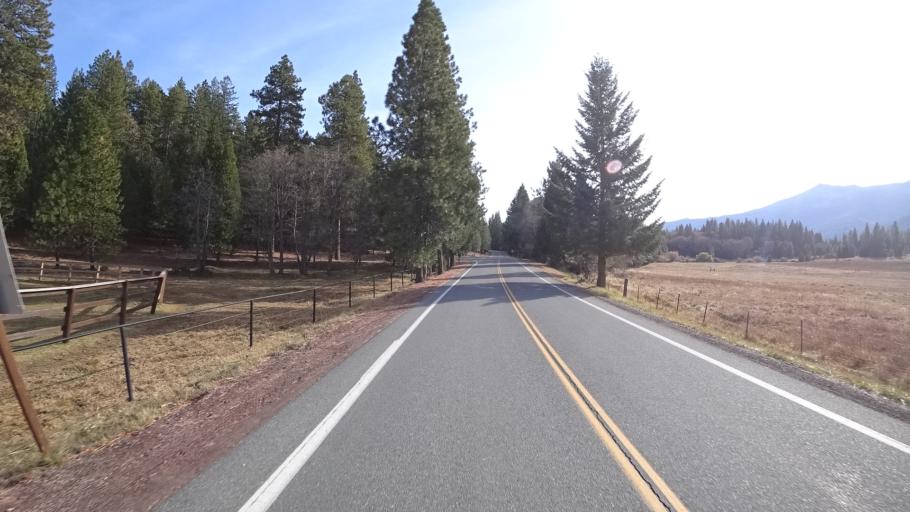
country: US
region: California
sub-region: Siskiyou County
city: Weed
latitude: 41.4003
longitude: -122.4209
